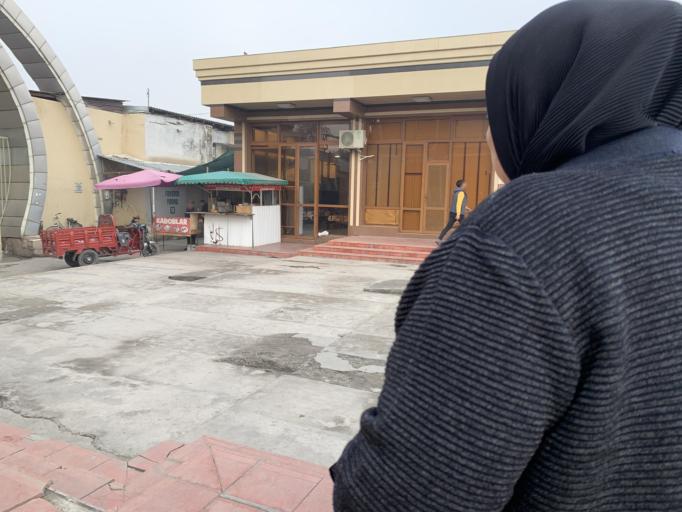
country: UZ
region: Fergana
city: Qo`qon
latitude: 40.5494
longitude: 70.9591
